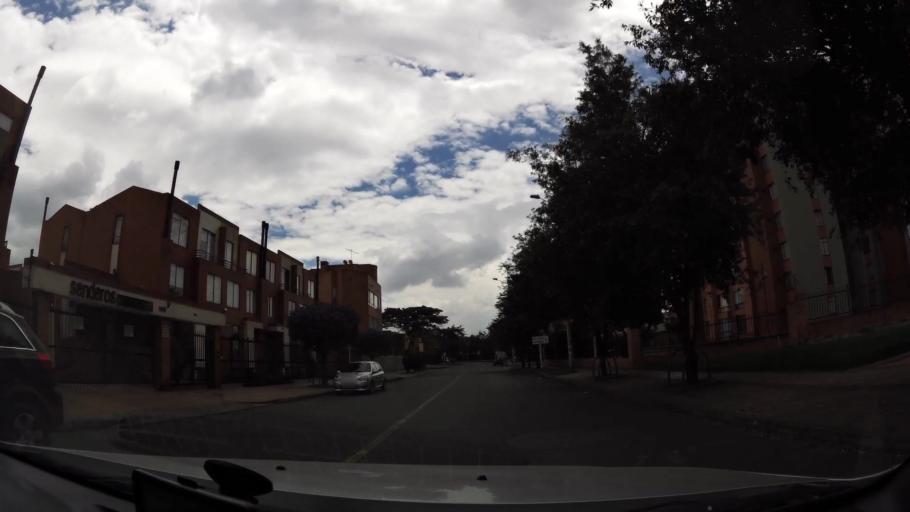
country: CO
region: Bogota D.C.
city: Bogota
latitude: 4.6356
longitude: -74.0984
